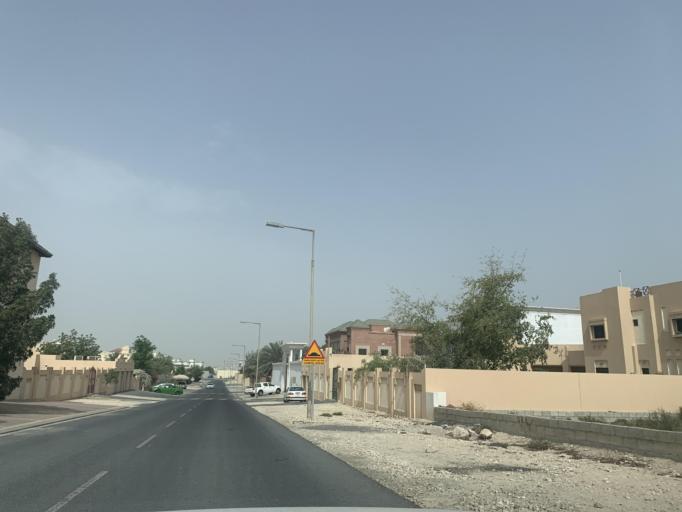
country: BH
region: Central Governorate
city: Madinat Hamad
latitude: 26.1457
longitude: 50.5160
